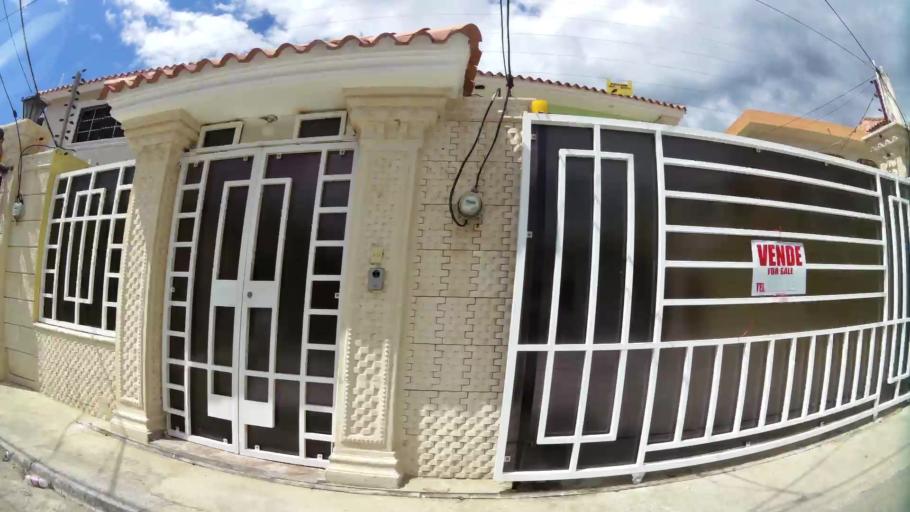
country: DO
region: San Cristobal
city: San Cristobal
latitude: 18.4178
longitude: -70.1021
